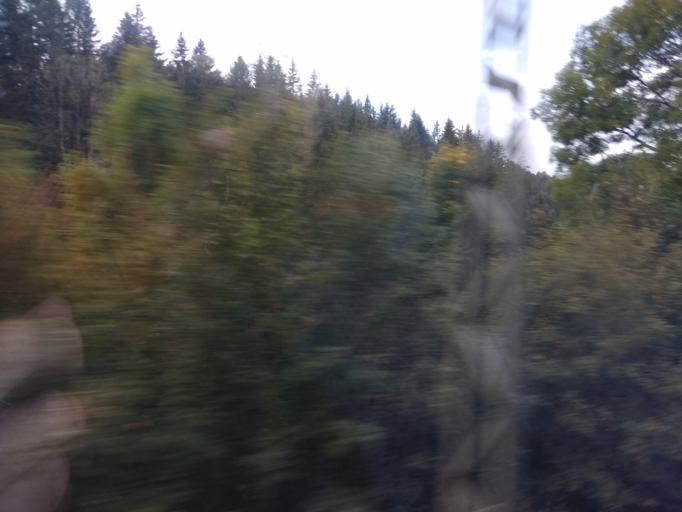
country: DE
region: Baden-Wuerttemberg
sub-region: Freiburg Region
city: Hinterzarten
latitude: 47.9104
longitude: 8.0949
